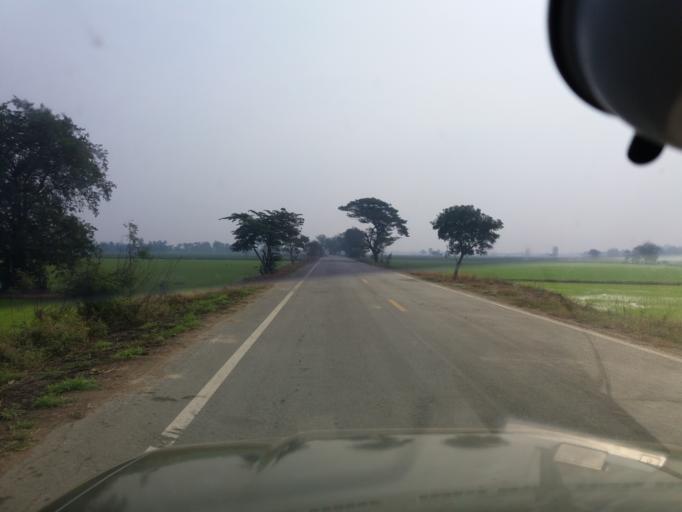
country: TH
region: Suphan Buri
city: Doem Bang Nang Buat
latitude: 14.8525
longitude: 100.1403
